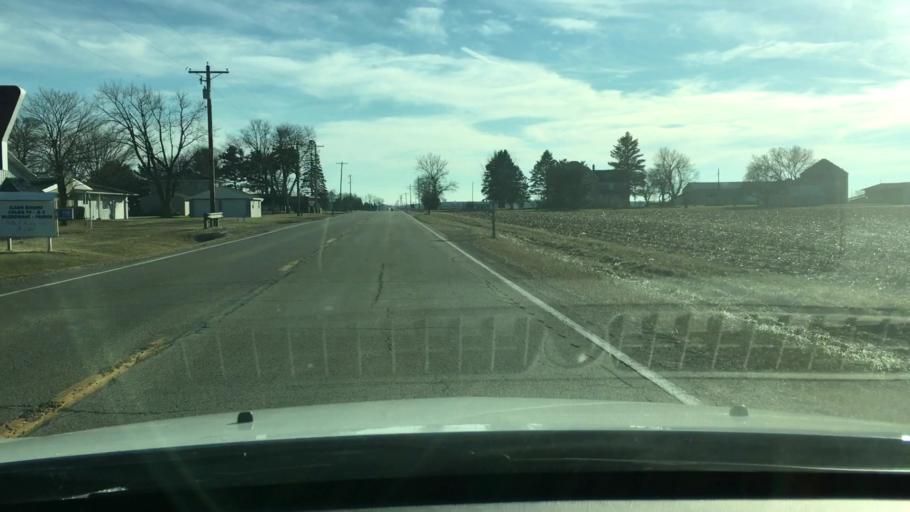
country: US
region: Illinois
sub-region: LaSalle County
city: Peru
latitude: 41.3960
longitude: -89.1260
